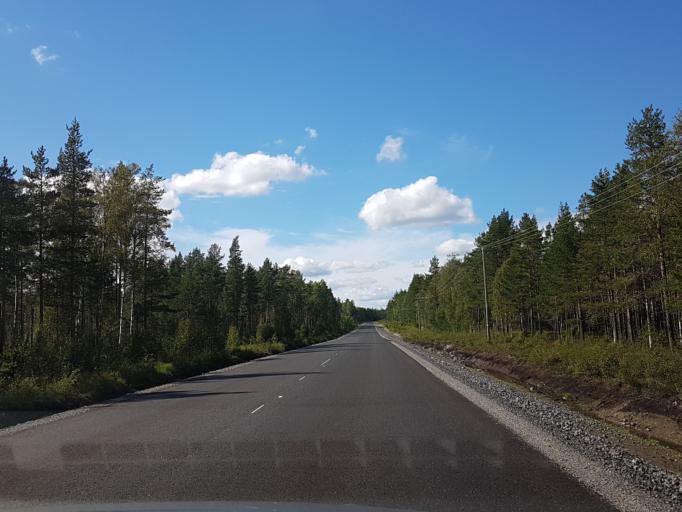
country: SE
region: Vaesterbotten
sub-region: Robertsfors Kommun
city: Robertsfors
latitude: 64.1229
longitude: 20.6803
